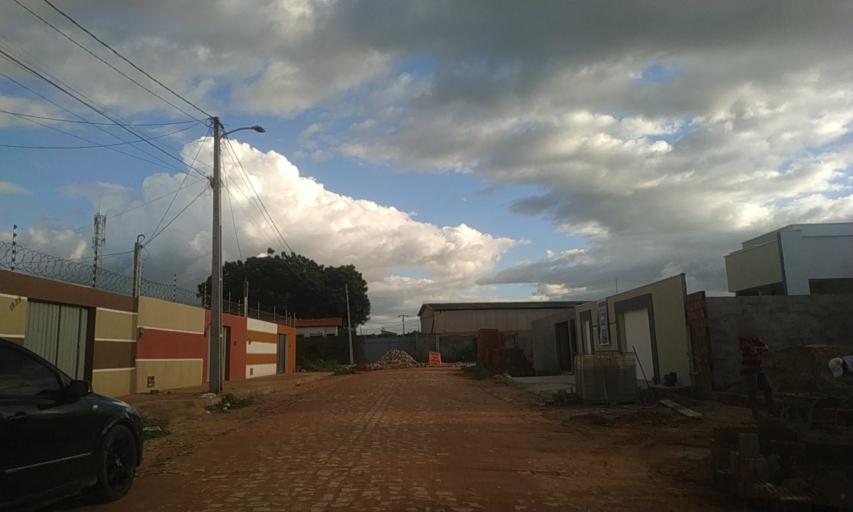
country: BR
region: Rio Grande do Norte
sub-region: Mossoro
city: Mossoro
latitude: -5.2228
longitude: -37.3436
